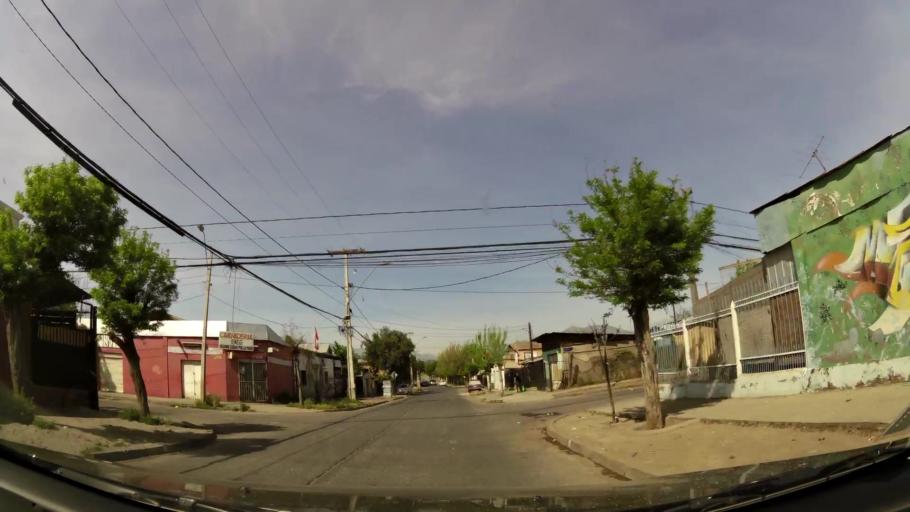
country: CL
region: Santiago Metropolitan
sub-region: Provincia de Cordillera
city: Puente Alto
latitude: -33.6218
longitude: -70.5808
